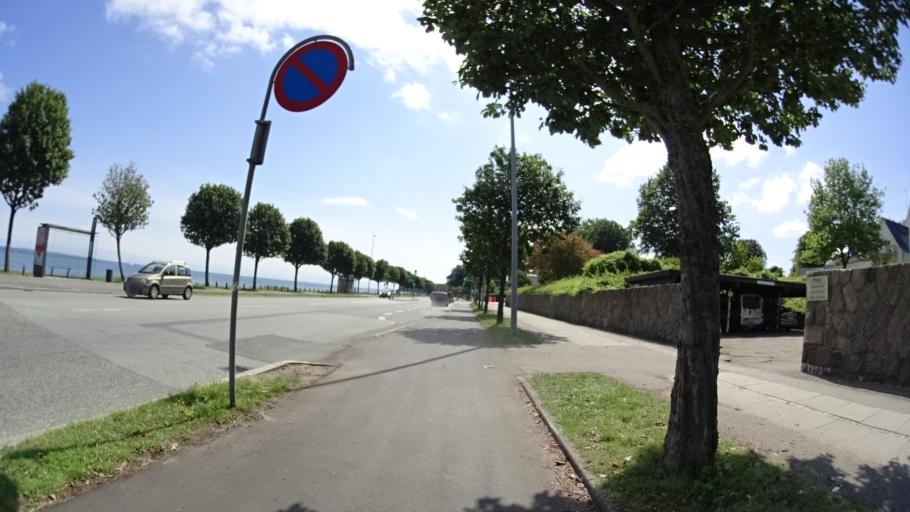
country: DK
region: Central Jutland
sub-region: Arhus Kommune
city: Arhus
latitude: 56.1355
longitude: 10.2087
